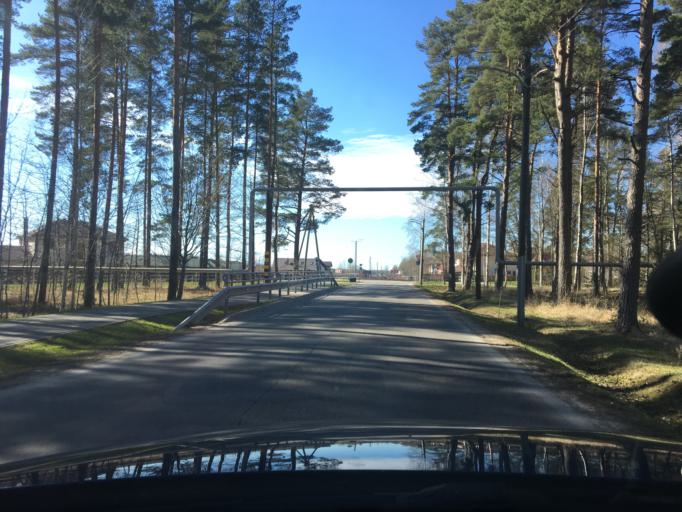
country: LV
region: Salaspils
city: Salaspils
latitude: 56.8717
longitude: 24.3419
